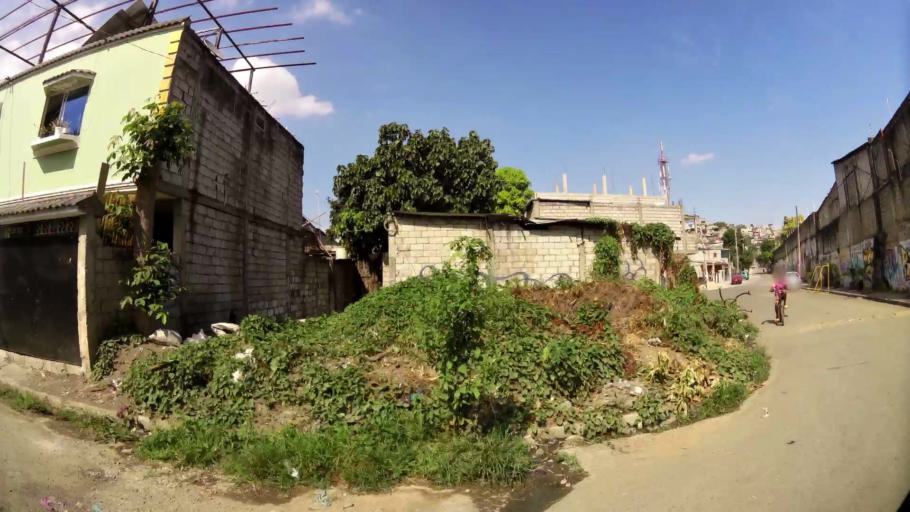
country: EC
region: Guayas
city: Guayaquil
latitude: -2.1506
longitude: -79.9411
